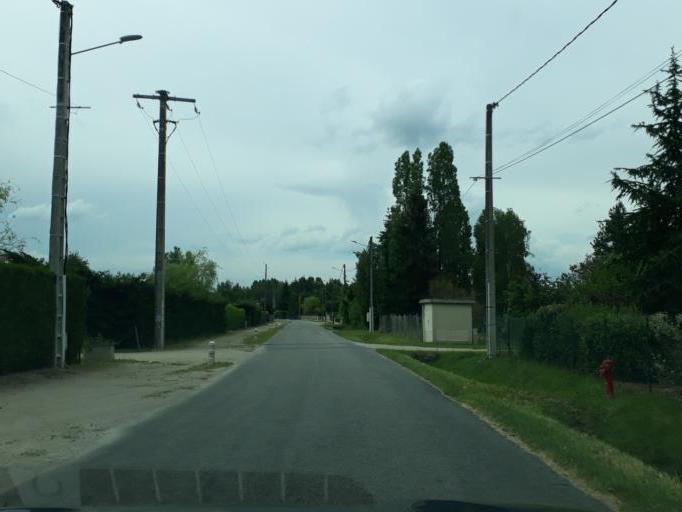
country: FR
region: Centre
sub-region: Departement du Loiret
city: Tigy
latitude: 47.7886
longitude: 2.2088
